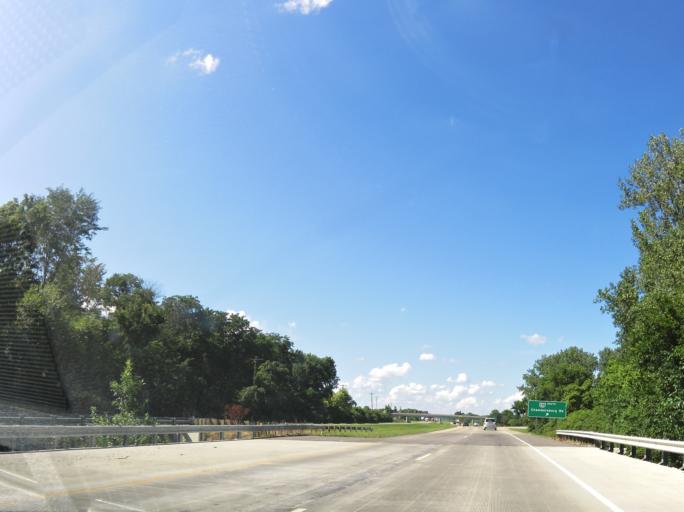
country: US
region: Ohio
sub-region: Greene County
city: Wright-Patterson AFB
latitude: 39.8401
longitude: -84.0596
